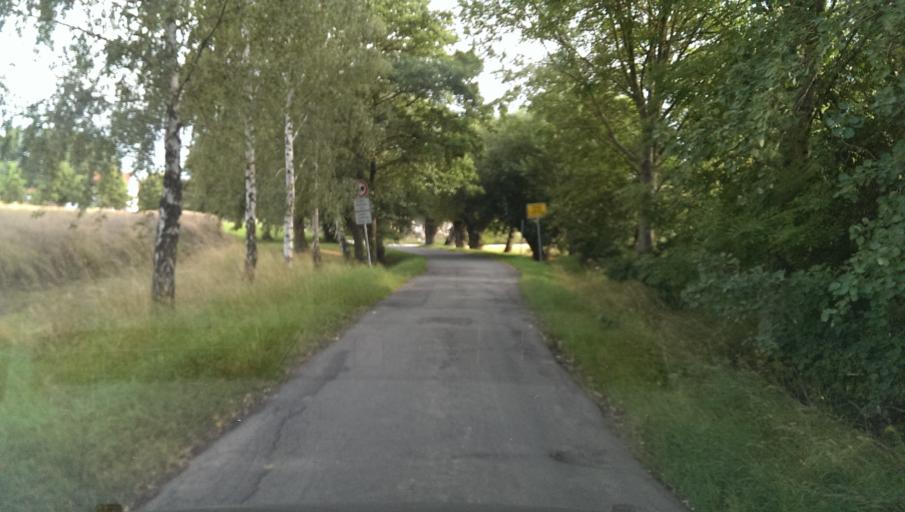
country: DE
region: Thuringia
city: Hirschfeld
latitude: 50.9321
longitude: 12.1801
